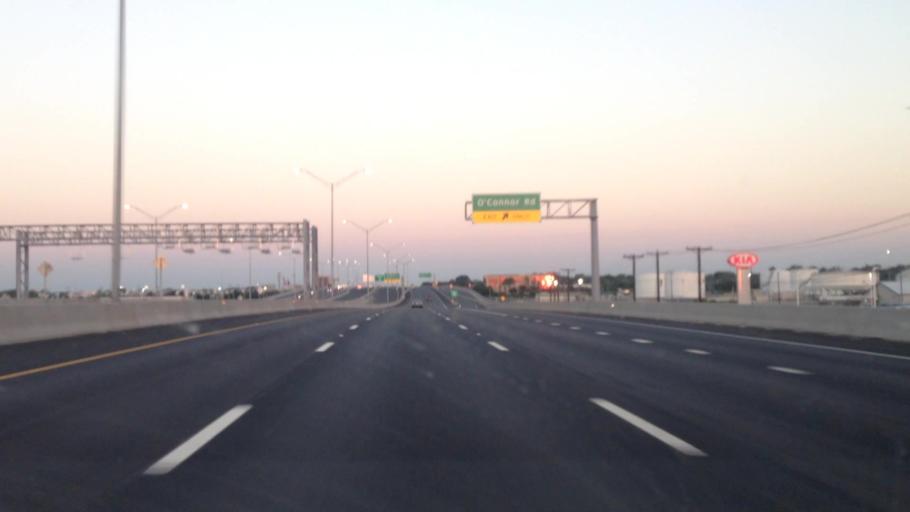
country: US
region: Texas
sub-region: Dallas County
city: Irving
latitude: 32.8375
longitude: -96.9312
